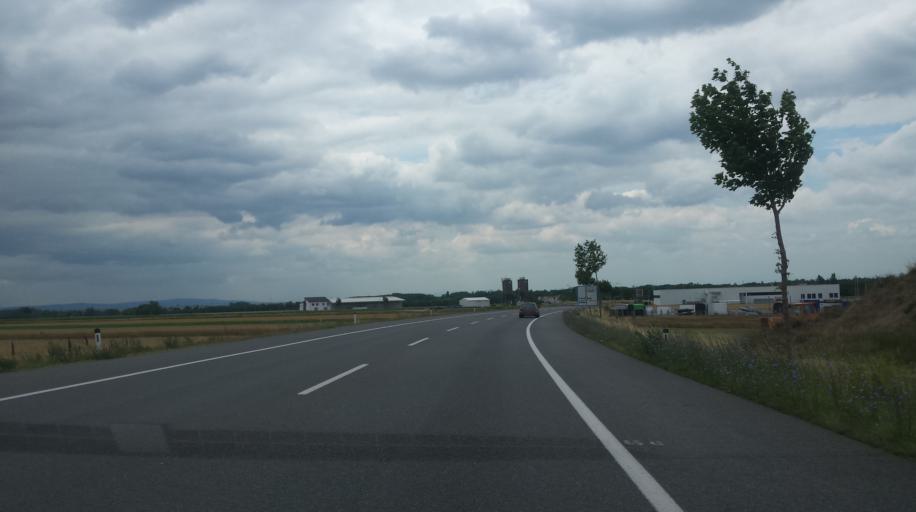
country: AT
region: Lower Austria
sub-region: Politischer Bezirk Wien-Umgebung
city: Himberg
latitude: 48.0744
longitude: 16.4612
